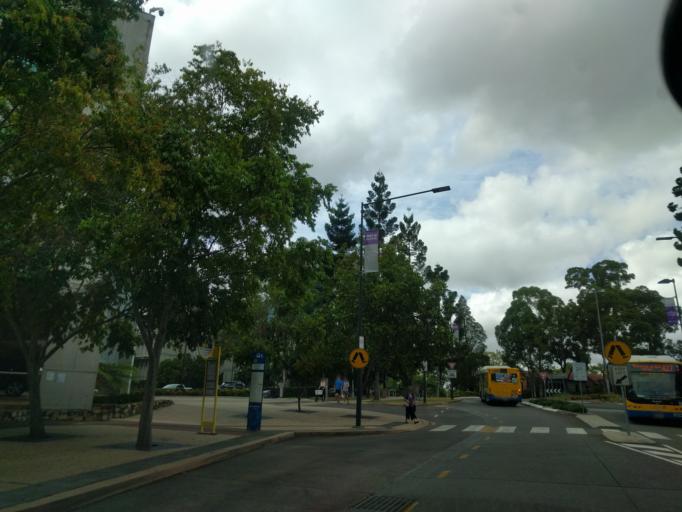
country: AU
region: Queensland
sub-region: Brisbane
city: Yeronga
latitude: -27.4983
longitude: 153.0110
